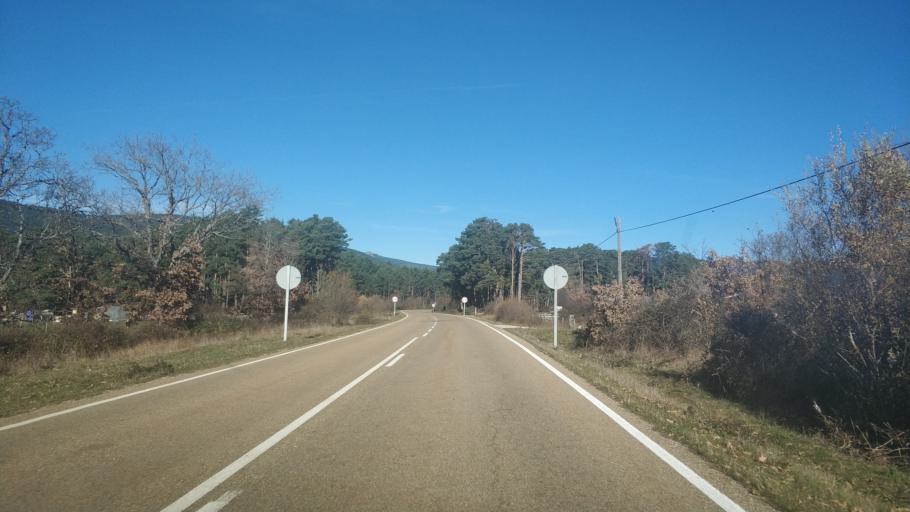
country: ES
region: Castille and Leon
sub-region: Provincia de Soria
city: Vinuesa
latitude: 41.9222
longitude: -2.7611
